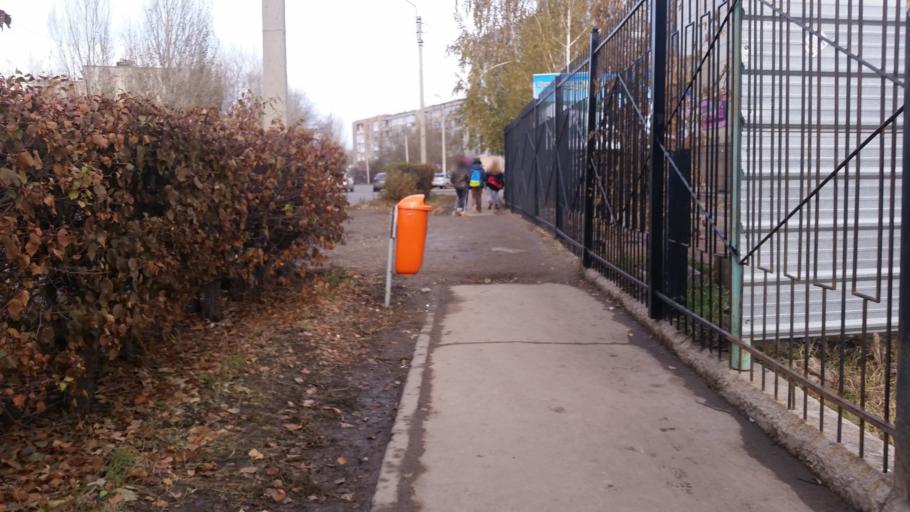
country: KZ
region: Astana Qalasy
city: Astana
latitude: 51.1535
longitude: 71.4743
